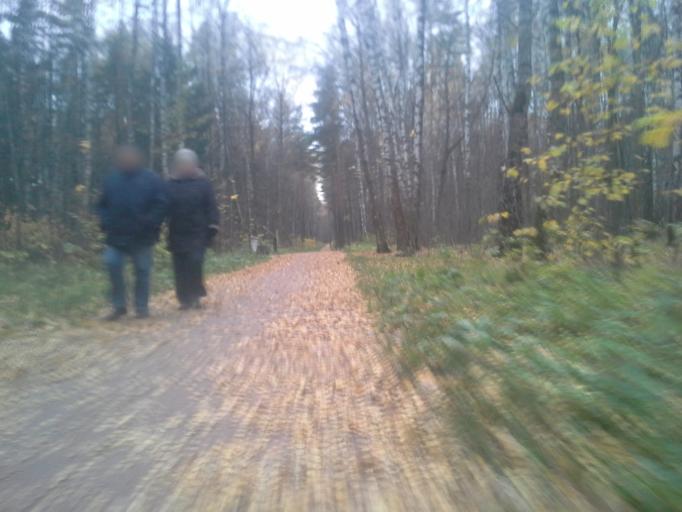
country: RU
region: Moskovskaya
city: Zarech'ye
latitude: 55.6659
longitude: 37.3970
